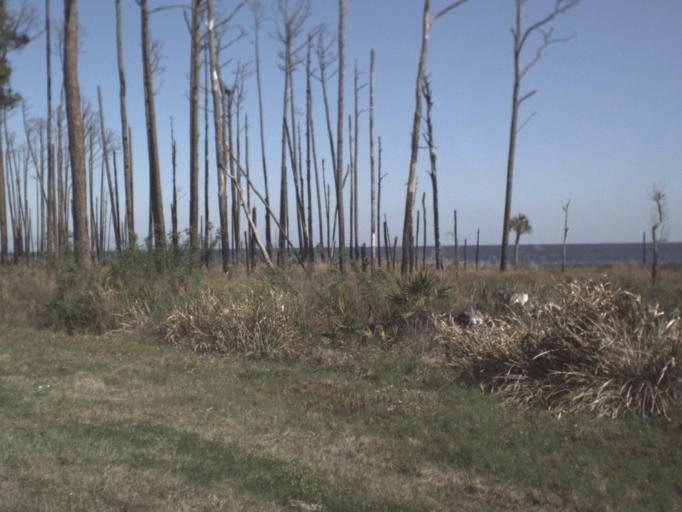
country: US
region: Florida
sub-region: Franklin County
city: Carrabelle
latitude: 29.8615
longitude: -84.6254
